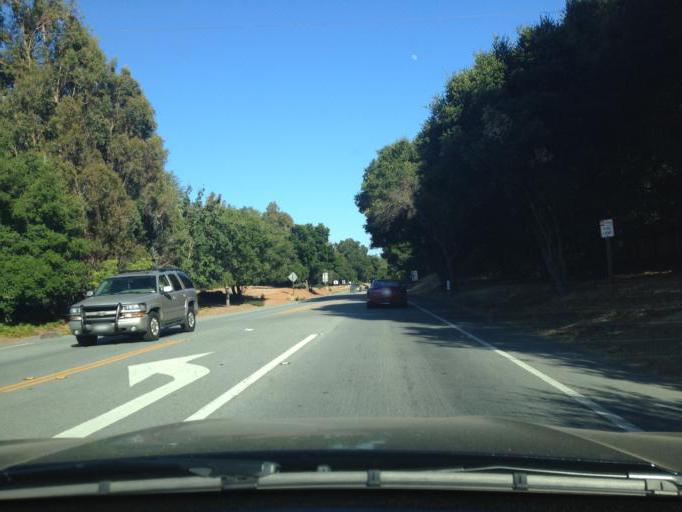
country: US
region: California
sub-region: Santa Clara County
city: Saratoga
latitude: 37.2539
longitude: -122.0255
